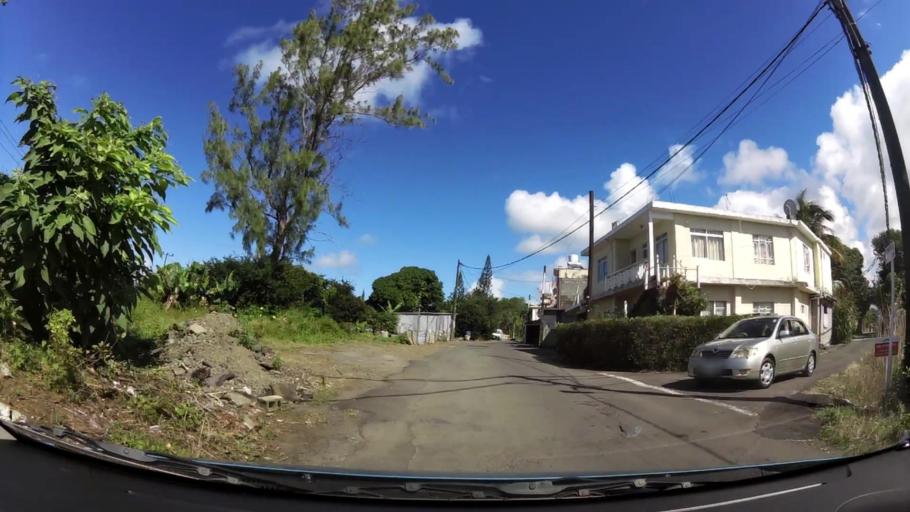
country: MU
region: Grand Port
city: Plaine Magnien
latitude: -20.4291
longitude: 57.6708
